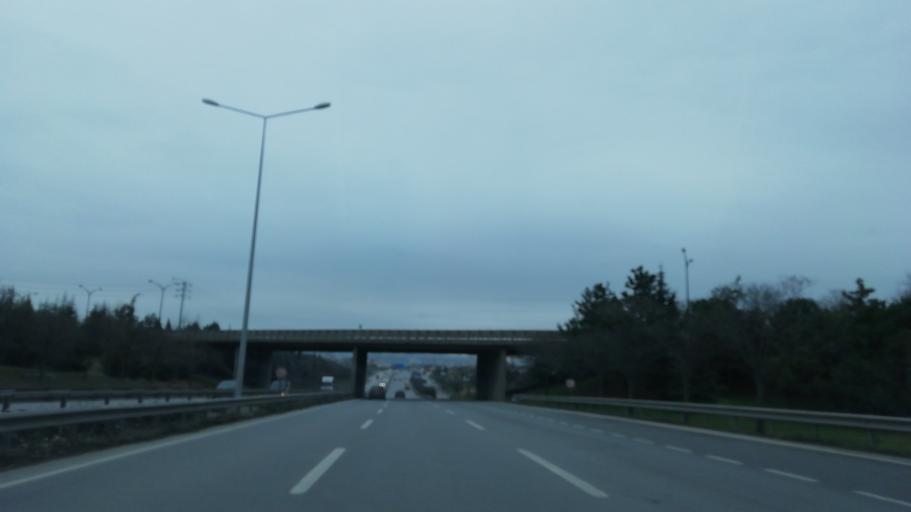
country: TR
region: Kocaeli
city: Gebze
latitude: 40.8019
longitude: 29.4723
